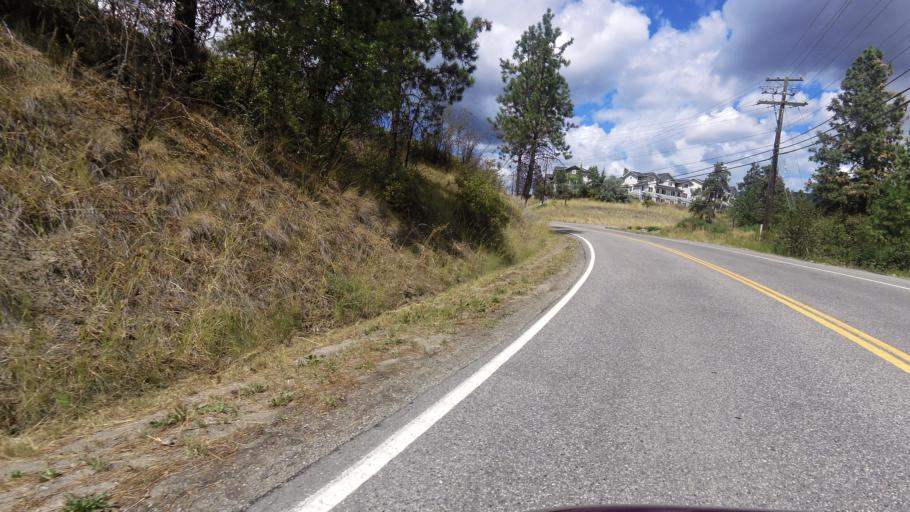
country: CA
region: British Columbia
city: West Kelowna
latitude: 49.8268
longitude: -119.6178
